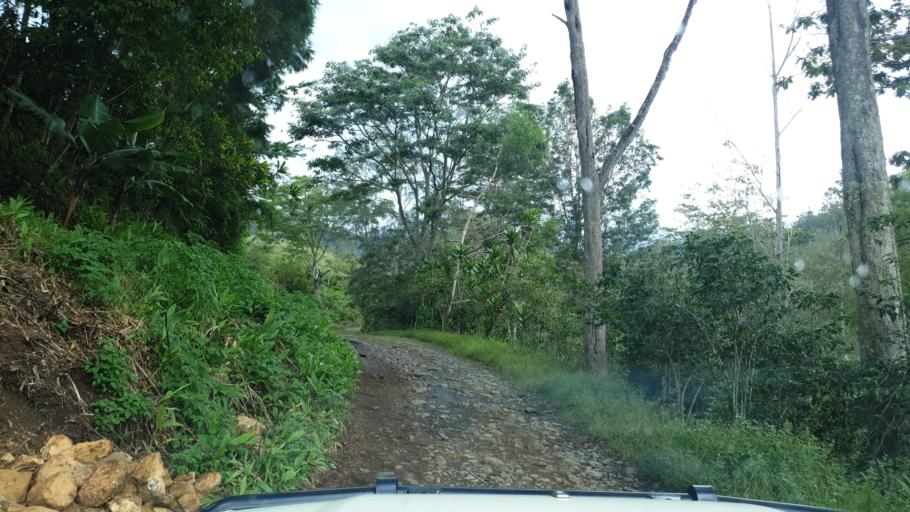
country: PG
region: Eastern Highlands
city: Goroka
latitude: -5.9203
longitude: 145.2588
